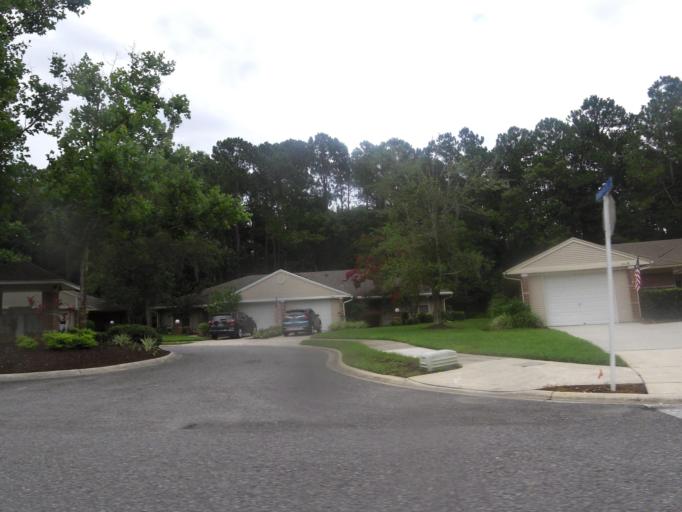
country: US
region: Florida
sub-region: Saint Johns County
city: Ponte Vedra Beach
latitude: 30.2559
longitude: -81.4550
